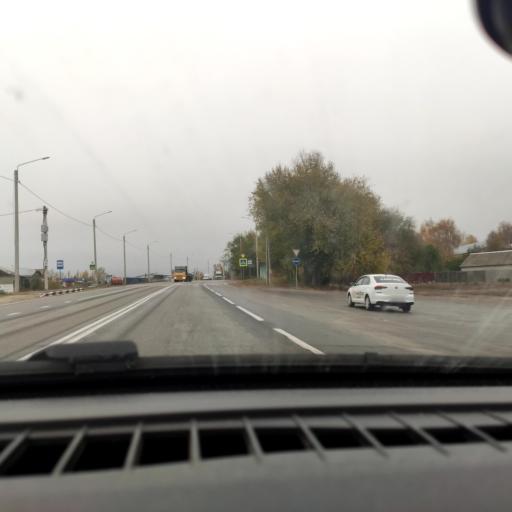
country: RU
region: Voronezj
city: Uryv-Pokrovka
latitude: 51.0430
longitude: 38.9820
